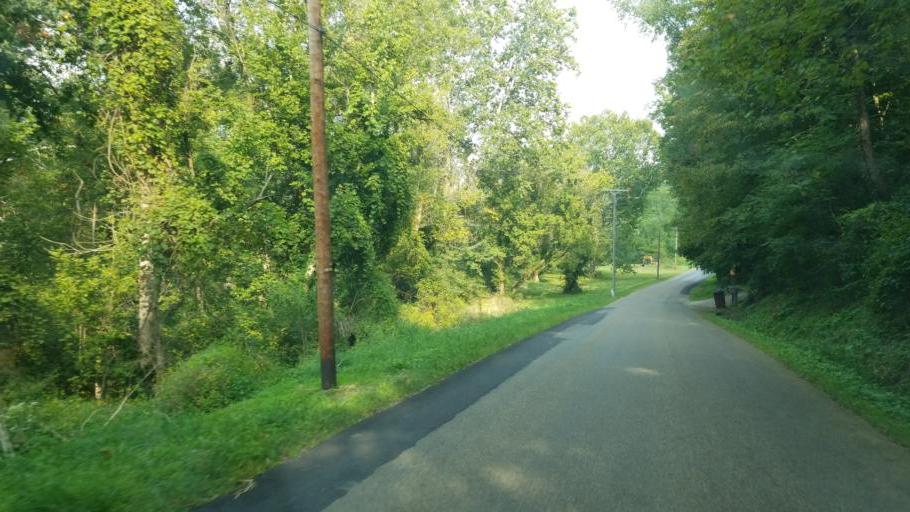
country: US
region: Ohio
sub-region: Knox County
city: Mount Vernon
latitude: 40.3714
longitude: -82.4607
